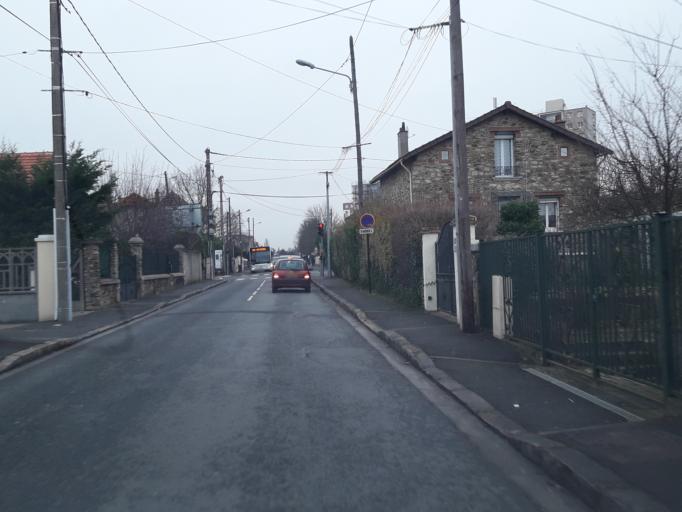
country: FR
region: Ile-de-France
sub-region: Departement de l'Essonne
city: Morsang-sur-Orge
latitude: 48.6625
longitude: 2.3579
